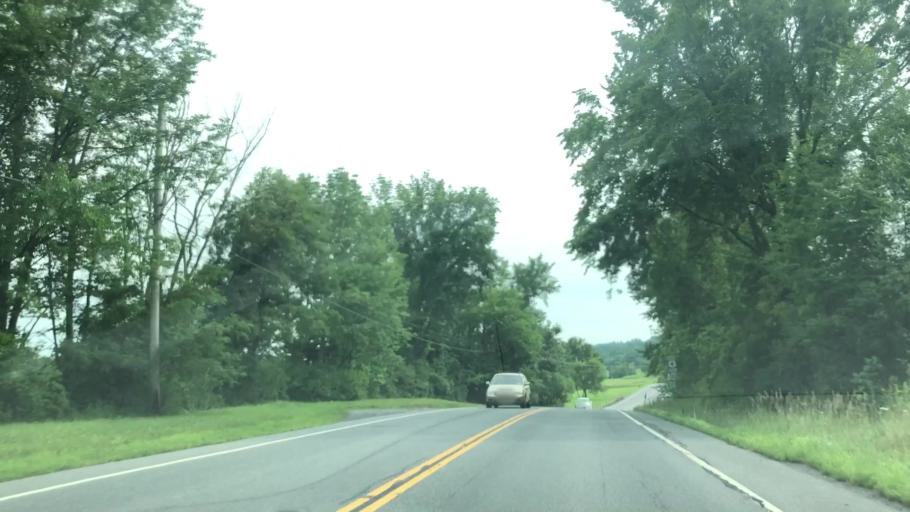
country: US
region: New York
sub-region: Washington County
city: Whitehall
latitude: 43.5006
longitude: -73.4244
